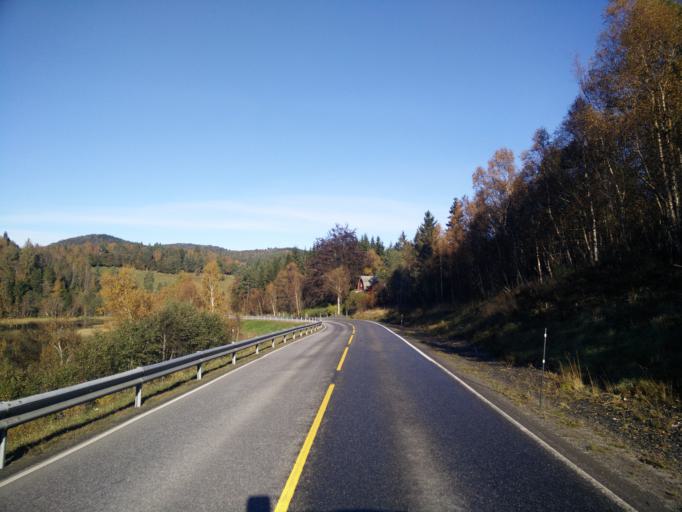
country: NO
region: More og Romsdal
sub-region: Tingvoll
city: Tingvoll
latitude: 63.0271
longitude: 8.0233
